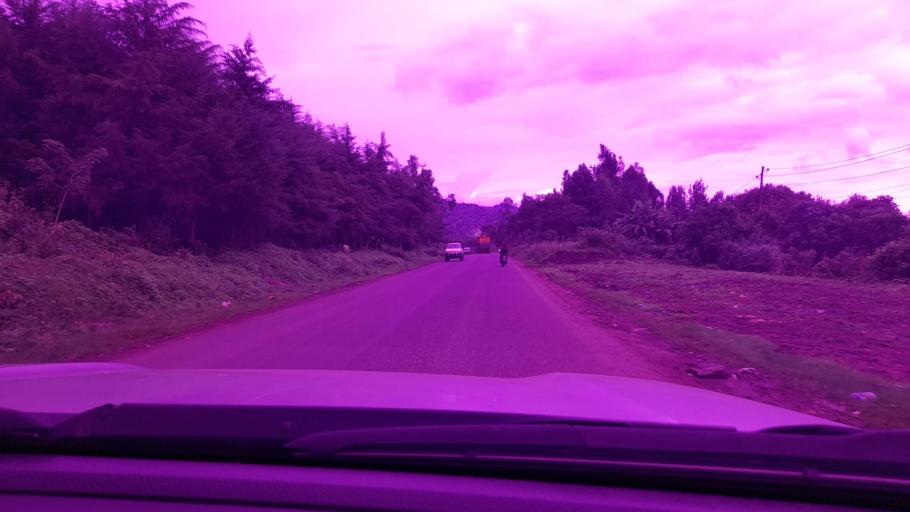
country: ET
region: Oromiya
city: Jima
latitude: 7.6633
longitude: 36.8739
